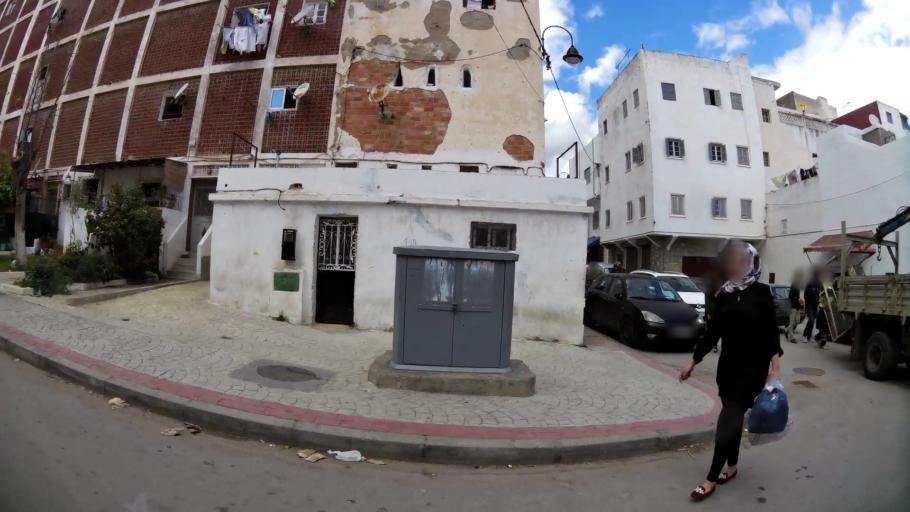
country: MA
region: Tanger-Tetouan
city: Tetouan
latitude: 35.5754
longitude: -5.3559
